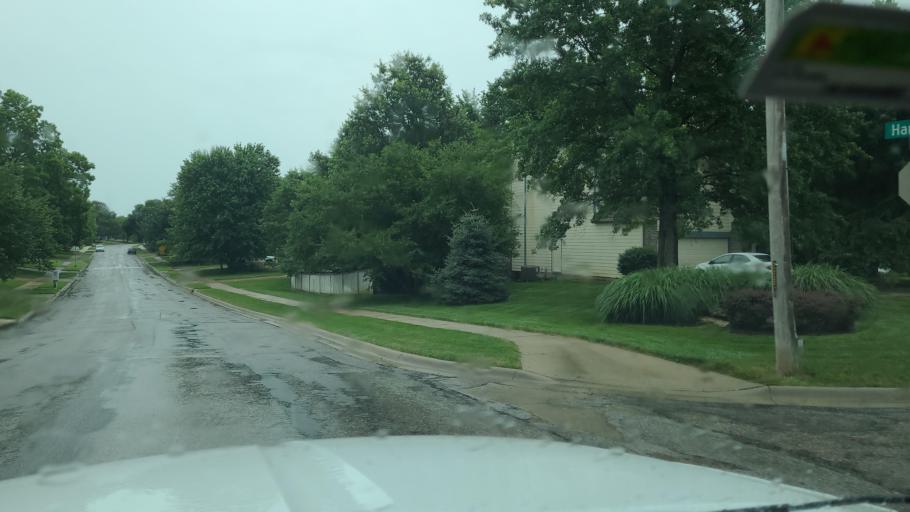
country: US
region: Kansas
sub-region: Douglas County
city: Lawrence
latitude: 38.9675
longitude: -95.3022
